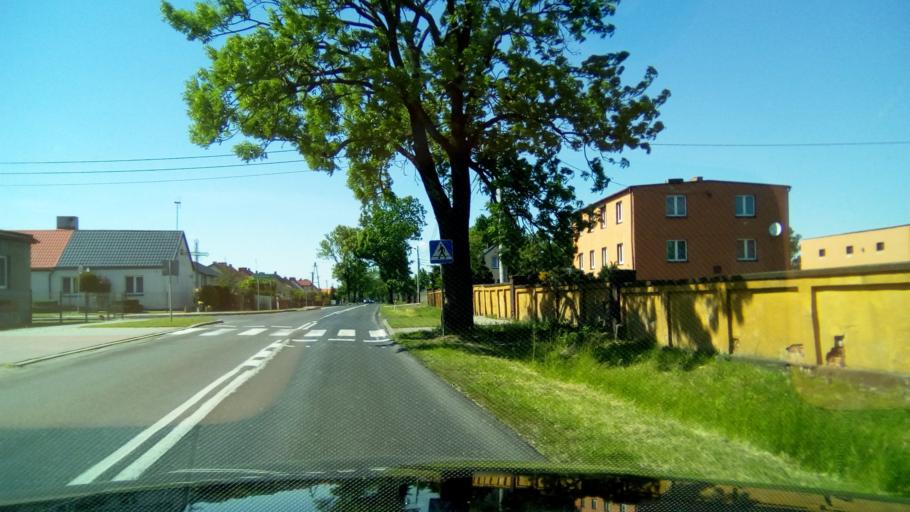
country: PL
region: Greater Poland Voivodeship
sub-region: Powiat gnieznienski
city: Niechanowo
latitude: 52.4812
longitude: 17.6629
